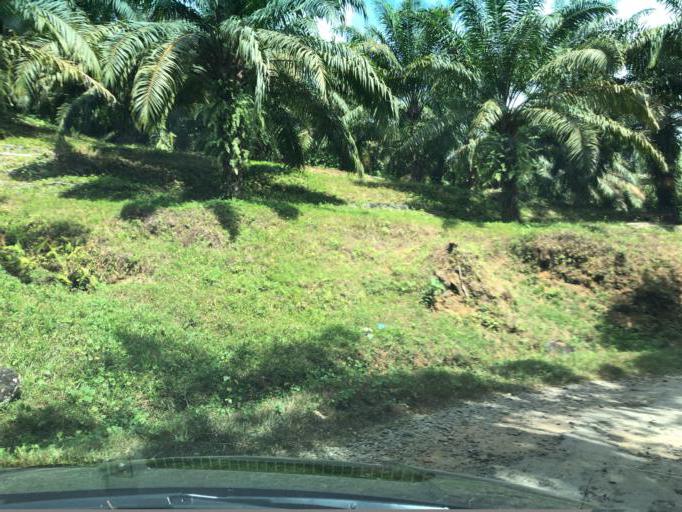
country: LK
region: Western
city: Horawala Junction
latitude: 6.5437
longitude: 80.0957
